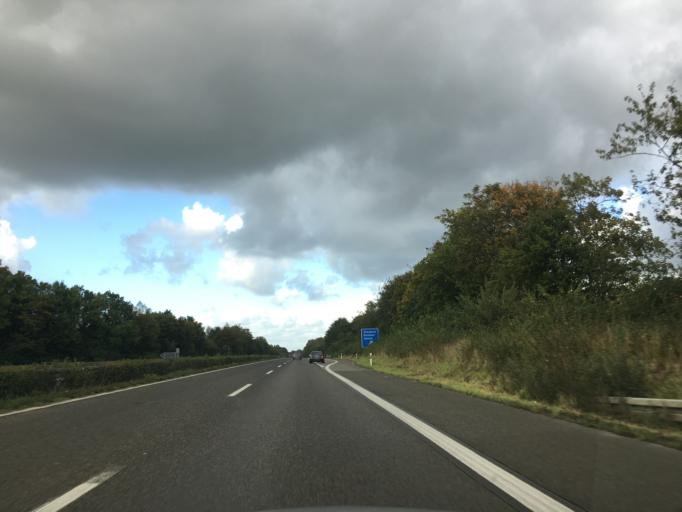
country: DE
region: North Rhine-Westphalia
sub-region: Regierungsbezirk Dusseldorf
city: Sonsbeck
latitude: 51.6025
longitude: 6.3543
